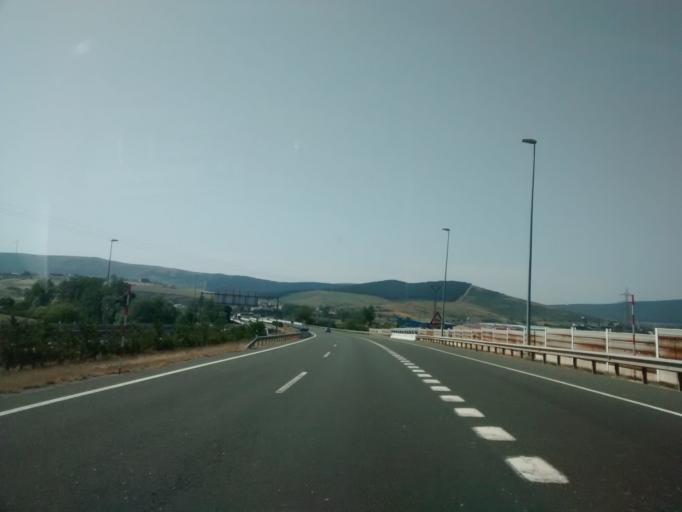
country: ES
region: Cantabria
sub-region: Provincia de Cantabria
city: Reinosa
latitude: 43.0046
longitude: -4.1264
